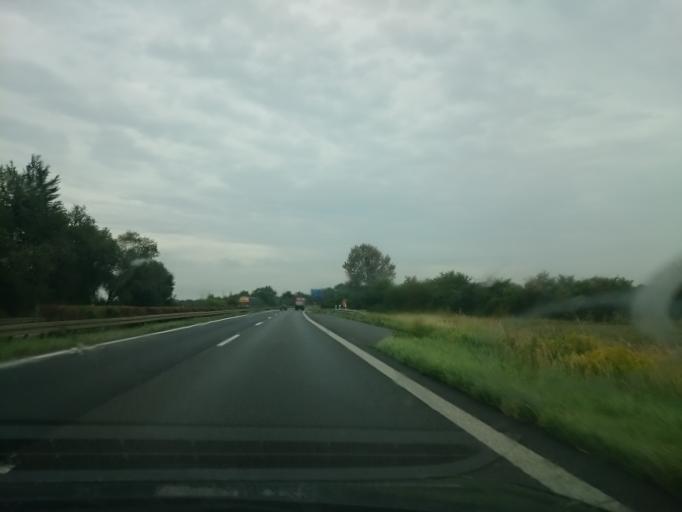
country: DE
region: Brandenburg
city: Wustermark
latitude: 52.4878
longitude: 12.9635
